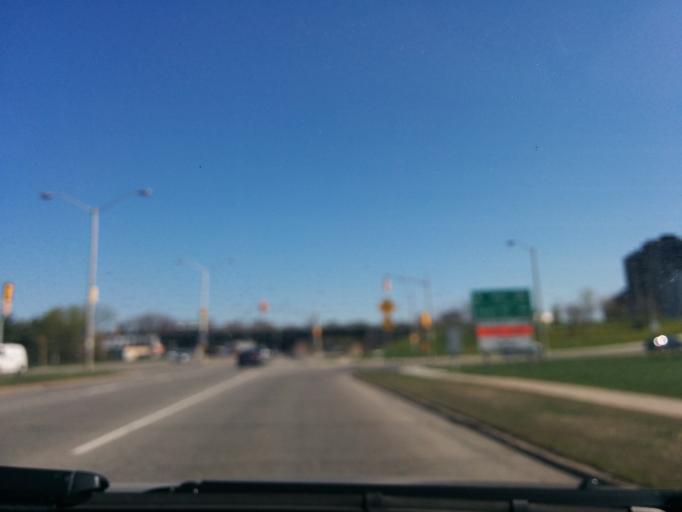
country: CA
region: Ontario
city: Ottawa
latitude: 45.3974
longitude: -75.6699
